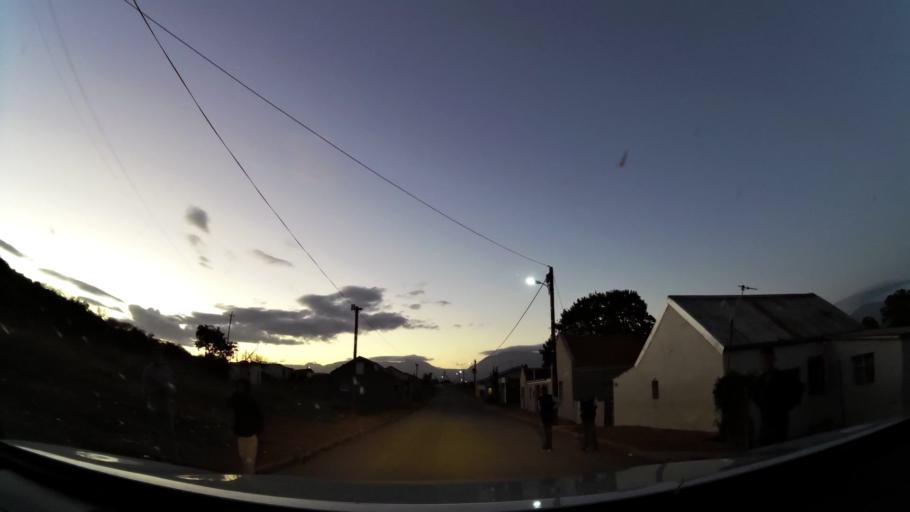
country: ZA
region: Western Cape
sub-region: Eden District Municipality
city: Riversdale
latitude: -34.1063
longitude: 21.2739
